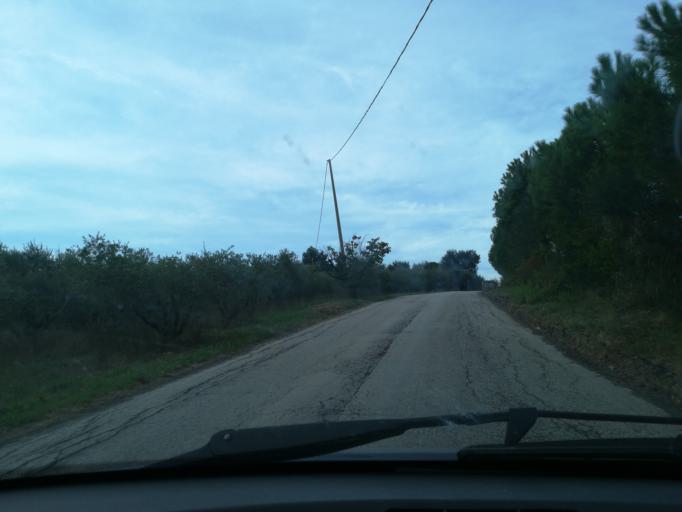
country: IT
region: The Marches
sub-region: Provincia di Macerata
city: Piediripa
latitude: 43.2891
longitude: 13.4883
